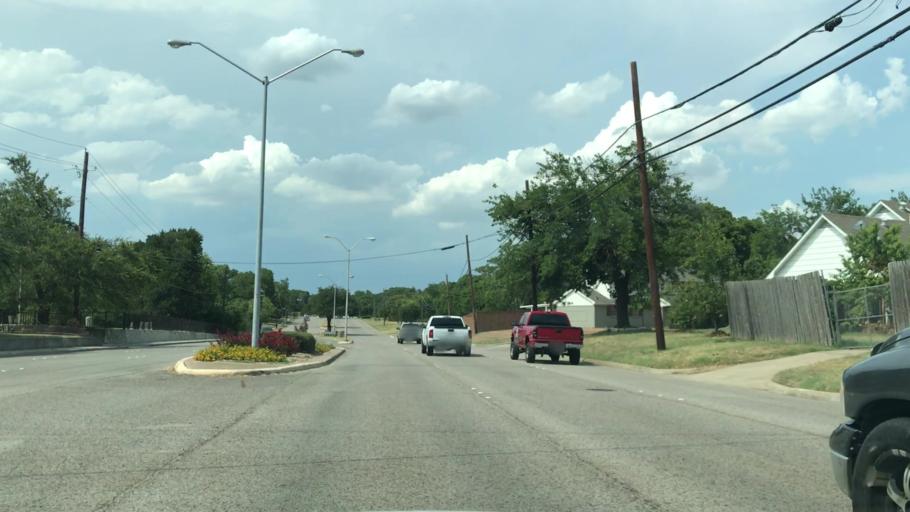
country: US
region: Texas
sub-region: Dallas County
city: Farmers Branch
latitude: 32.9170
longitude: -96.8731
